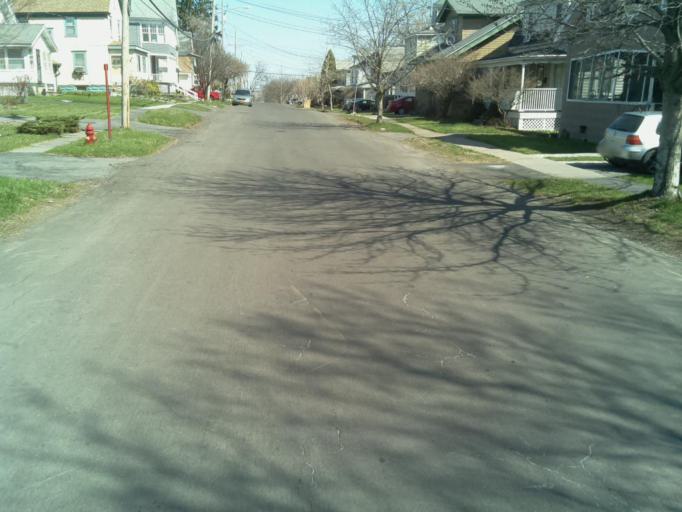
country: US
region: New York
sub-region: Onondaga County
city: Lyncourt
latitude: 43.0704
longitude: -76.1075
